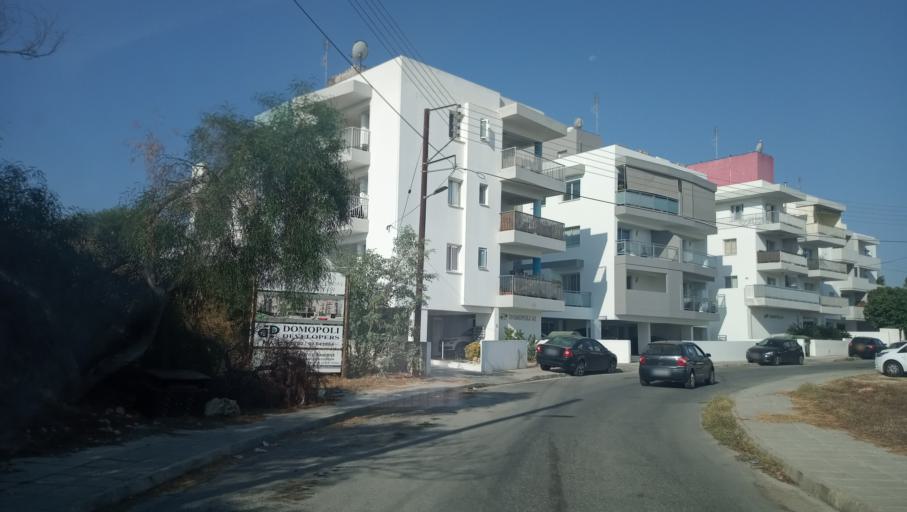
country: CY
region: Lefkosia
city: Geri
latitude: 35.1114
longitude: 33.4214
